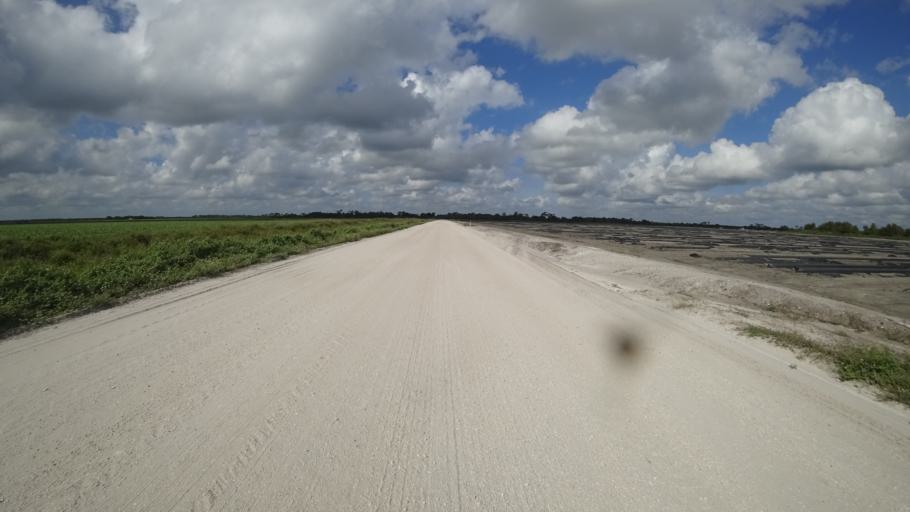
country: US
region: Florida
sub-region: Sarasota County
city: Lake Sarasota
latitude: 27.4129
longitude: -82.2049
